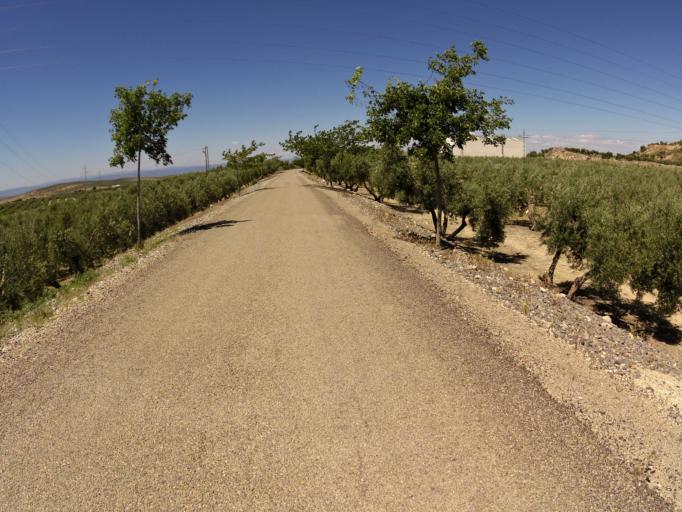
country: ES
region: Andalusia
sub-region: Provincia de Jaen
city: Torre del Campo
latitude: 37.7852
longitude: -3.8892
